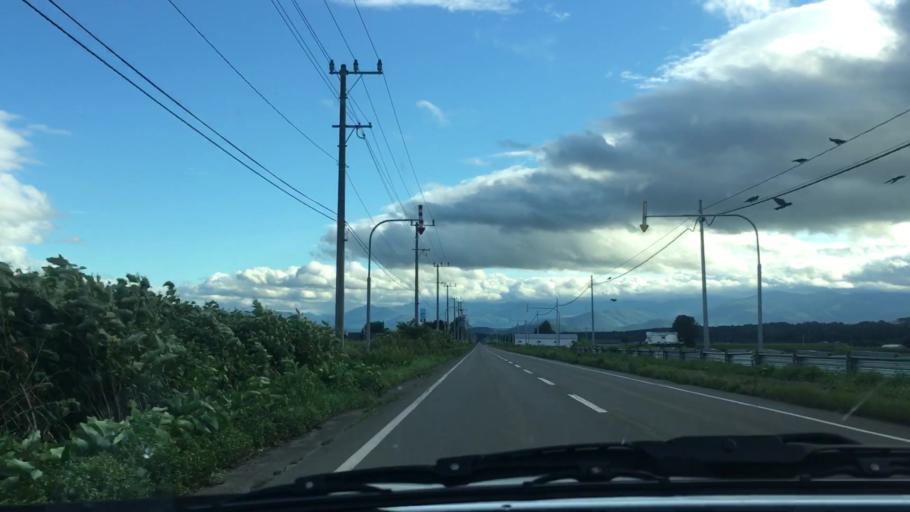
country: JP
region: Hokkaido
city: Otofuke
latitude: 43.1576
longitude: 142.9030
